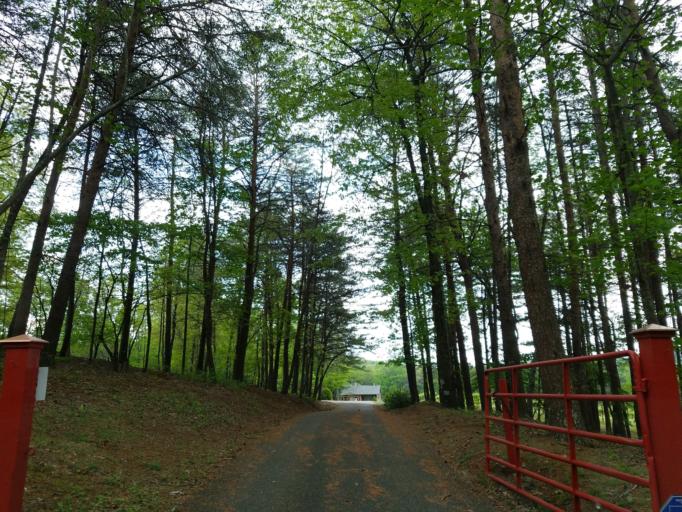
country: US
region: Georgia
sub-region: Pickens County
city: Jasper
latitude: 34.4411
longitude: -84.4877
